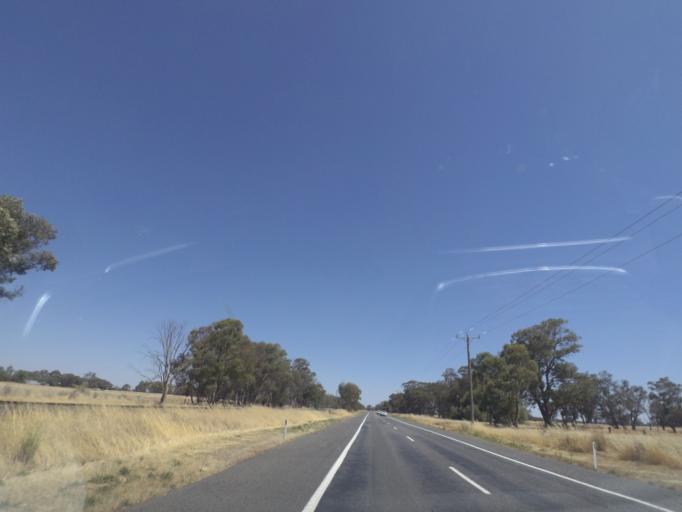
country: AU
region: Victoria
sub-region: Greater Shepparton
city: Shepparton
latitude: -36.2155
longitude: 145.4318
